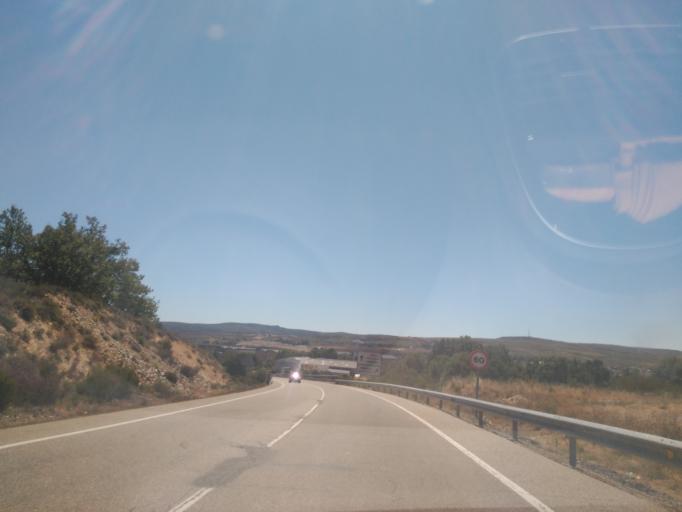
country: ES
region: Castille and Leon
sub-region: Provincia de Zamora
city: Puebla de Sanabria
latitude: 42.0644
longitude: -6.6223
